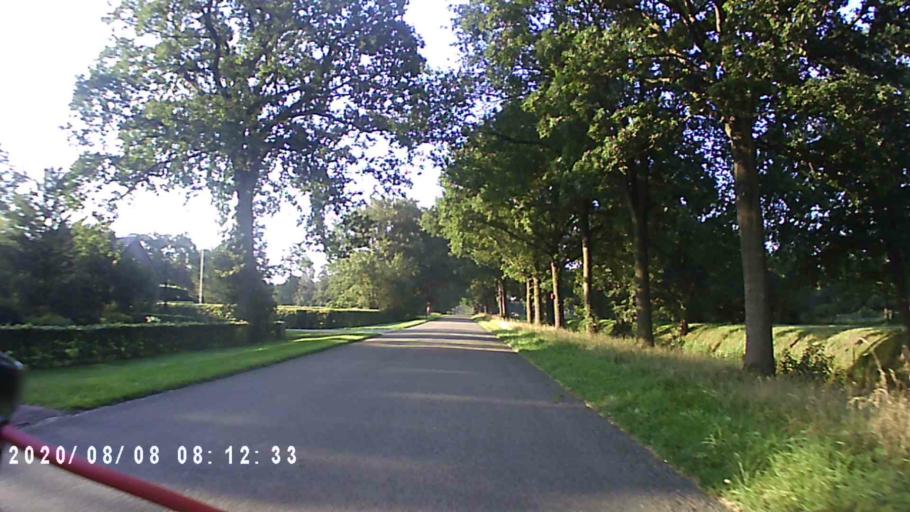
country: NL
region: Groningen
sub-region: Gemeente Leek
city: Leek
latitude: 53.1034
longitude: 6.3393
